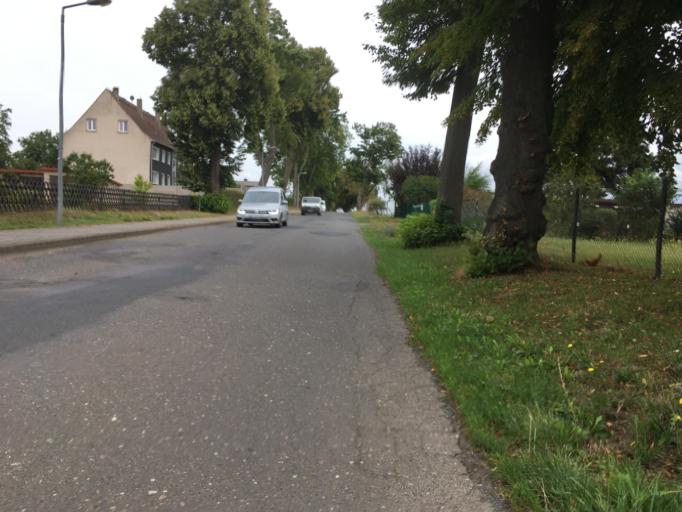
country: DE
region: Brandenburg
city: Prenzlau
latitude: 53.2310
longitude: 13.8431
